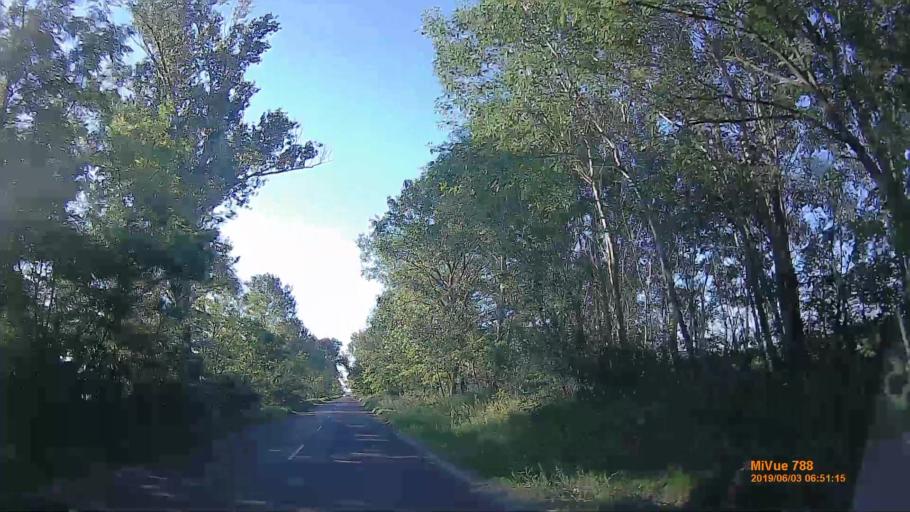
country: HU
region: Pest
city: Bugyi
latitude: 47.2129
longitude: 19.1822
